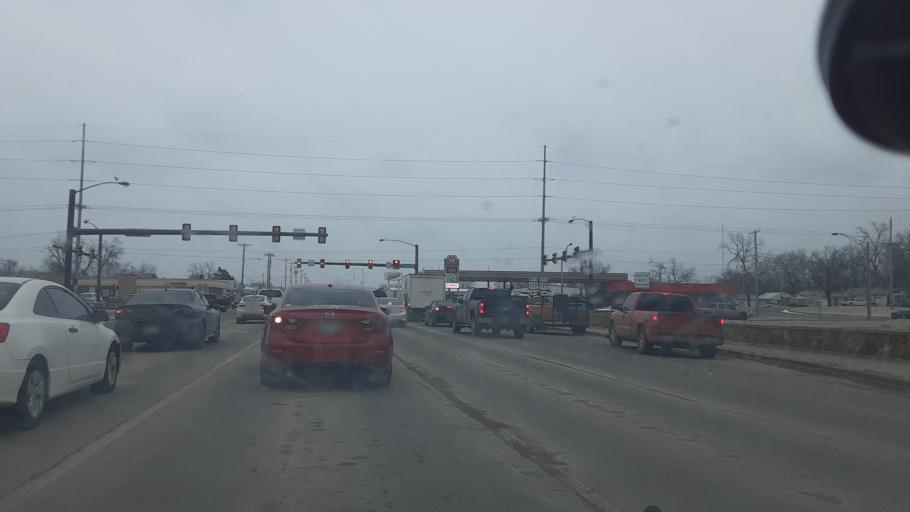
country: US
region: Oklahoma
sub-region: Payne County
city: Stillwater
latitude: 36.1160
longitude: -97.0523
